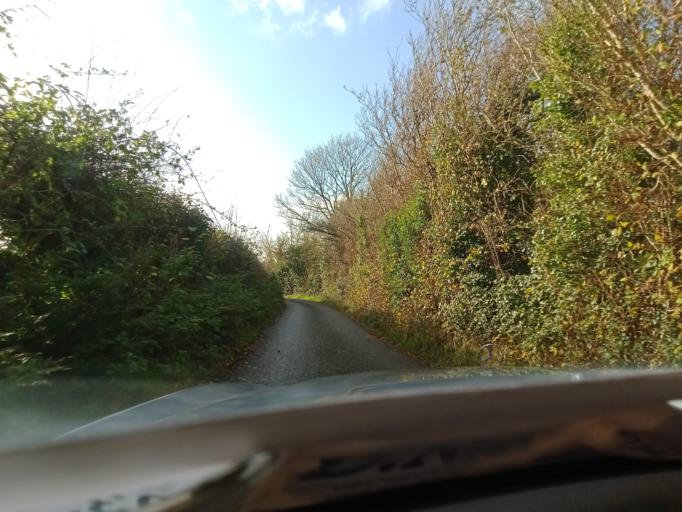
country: IE
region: Leinster
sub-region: Kilkenny
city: Mooncoin
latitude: 52.3091
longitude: -7.2769
